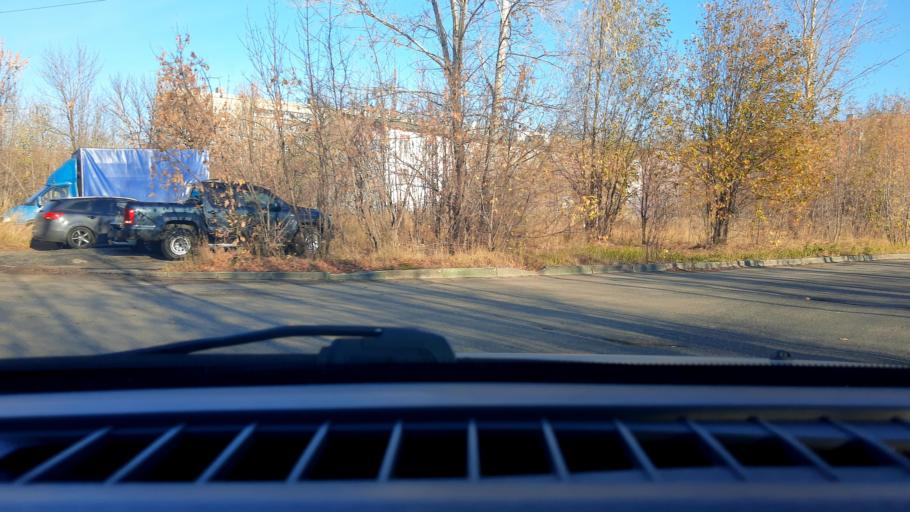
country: RU
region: Nizjnij Novgorod
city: Nizhniy Novgorod
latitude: 56.2549
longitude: 43.9196
